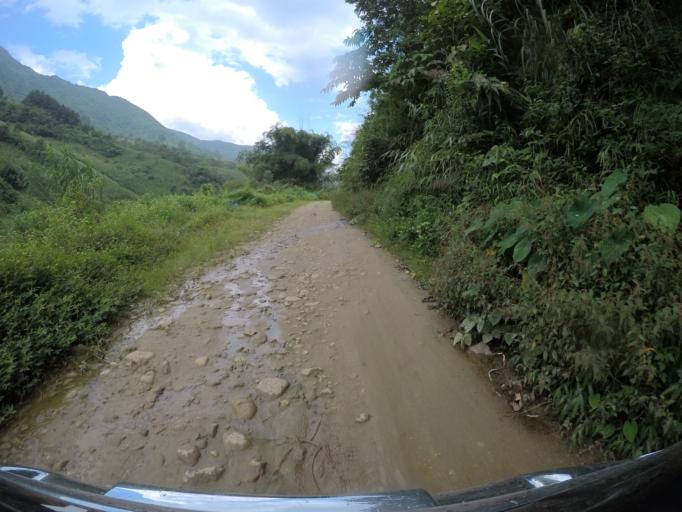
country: VN
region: Yen Bai
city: Son Thinh
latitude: 21.6694
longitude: 104.5197
